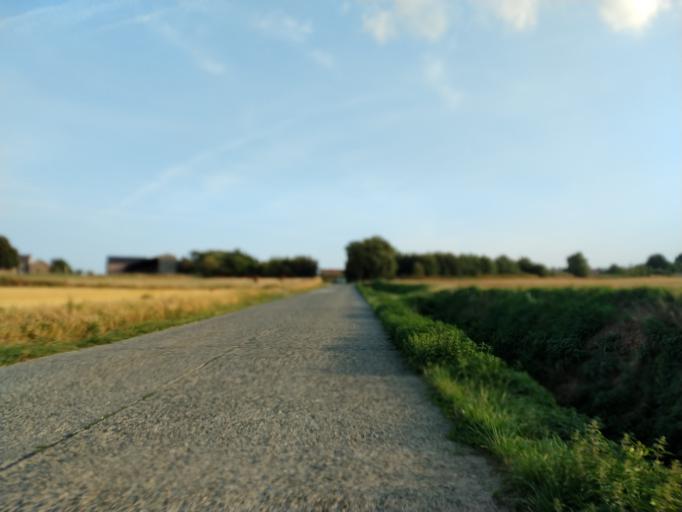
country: BE
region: Flanders
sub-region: Provincie Vlaams-Brabant
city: Hoegaarden
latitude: 50.7900
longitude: 4.8731
